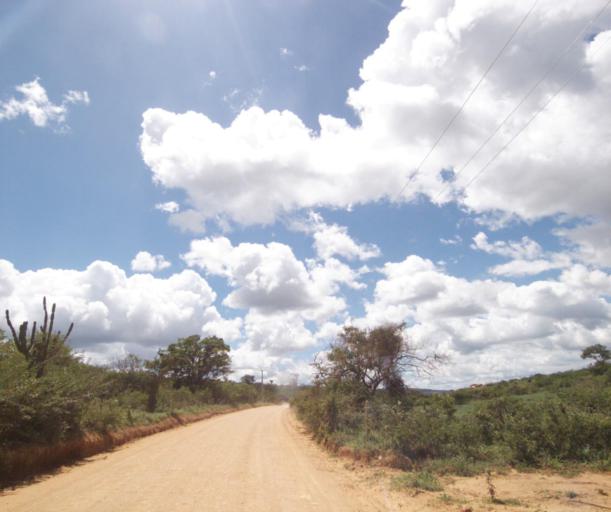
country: BR
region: Bahia
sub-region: Pocoes
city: Pocoes
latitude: -14.3586
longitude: -40.5836
